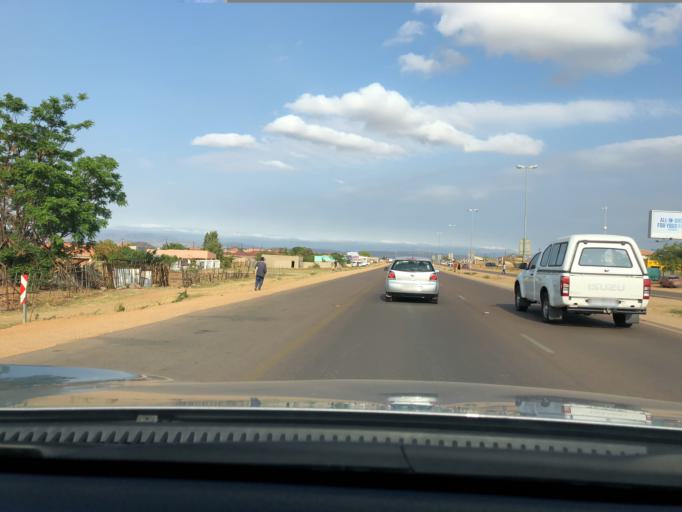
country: ZA
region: Limpopo
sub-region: Capricorn District Municipality
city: Mankoeng
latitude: -23.8893
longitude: 29.7023
